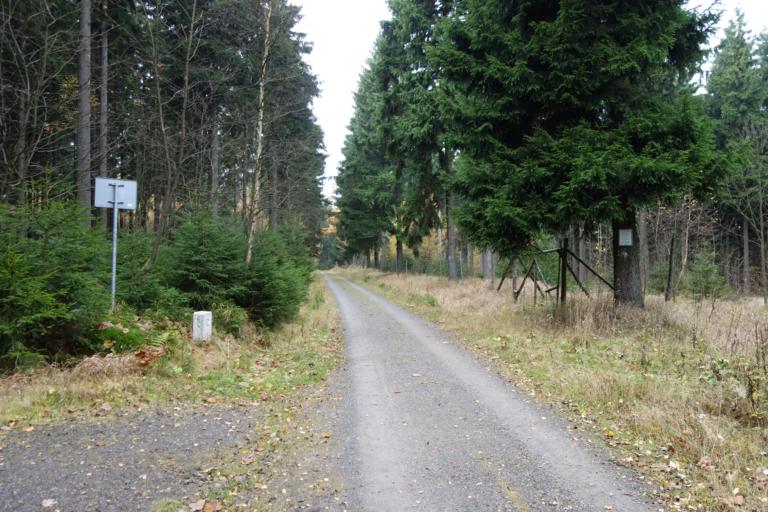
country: DE
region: Saxony
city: Pobershau
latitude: 50.5929
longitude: 13.2789
